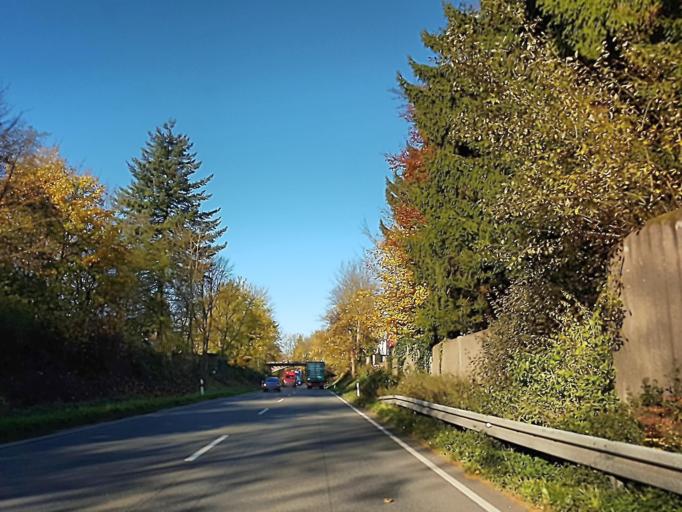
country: DE
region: North Rhine-Westphalia
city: Radevormwald
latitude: 51.1997
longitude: 7.3687
